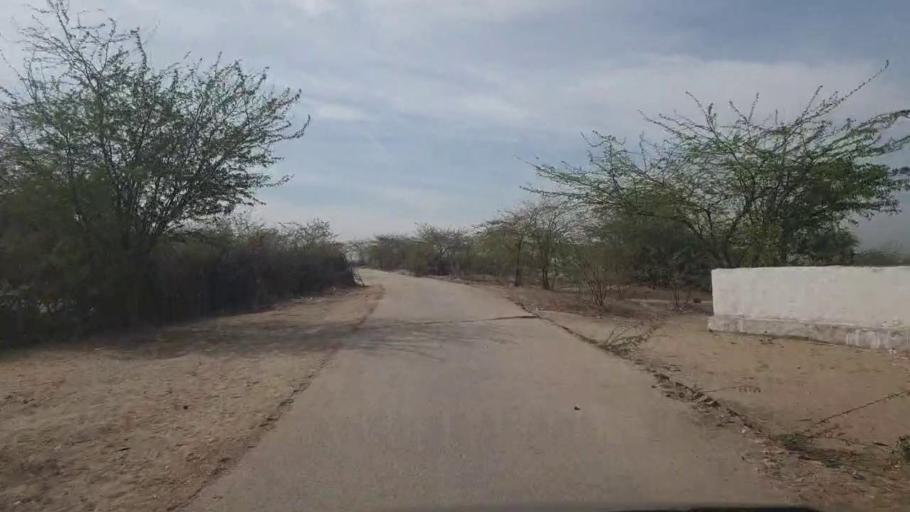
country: PK
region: Sindh
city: Umarkot
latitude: 25.2784
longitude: 69.7444
